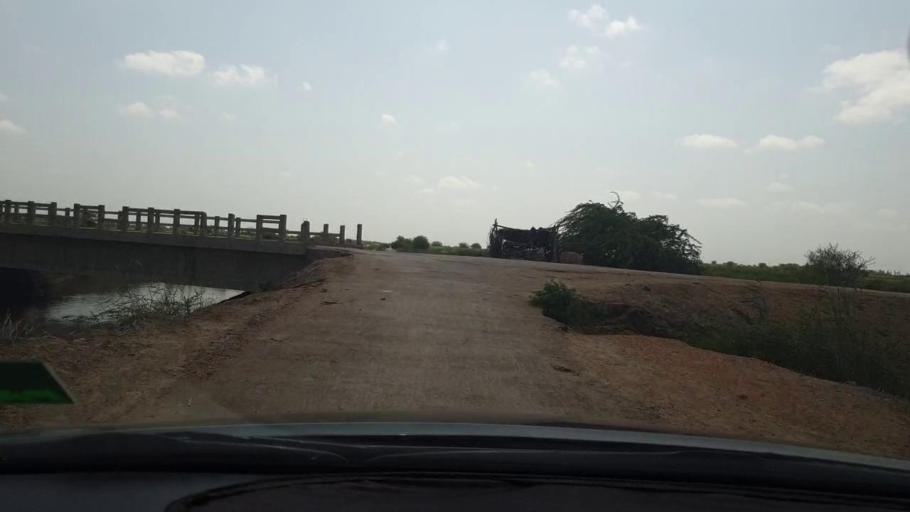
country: PK
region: Sindh
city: Tando Bago
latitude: 24.8252
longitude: 69.0662
